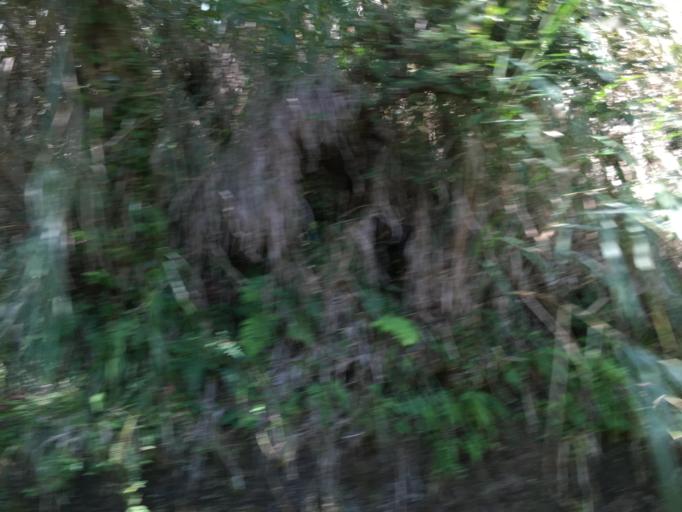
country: TW
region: Taiwan
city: Daxi
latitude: 24.5467
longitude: 121.4012
